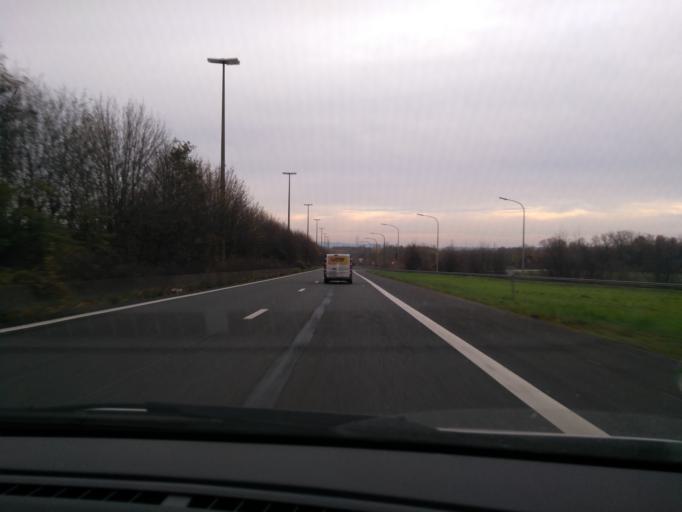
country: BE
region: Wallonia
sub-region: Province du Hainaut
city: Antoing
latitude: 50.5848
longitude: 3.4775
